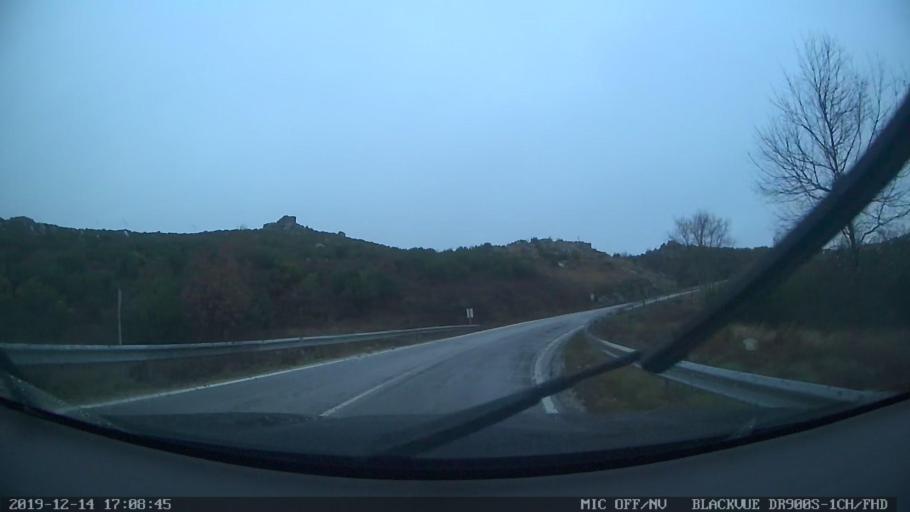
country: PT
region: Vila Real
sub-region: Vila Pouca de Aguiar
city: Vila Pouca de Aguiar
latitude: 41.4711
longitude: -7.6047
